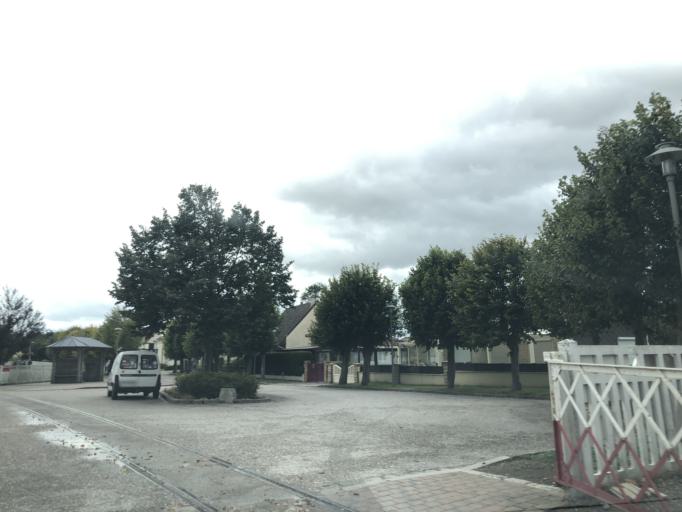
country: FR
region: Picardie
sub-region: Departement de la Somme
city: Le Crotoy
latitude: 50.2202
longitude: 1.6321
